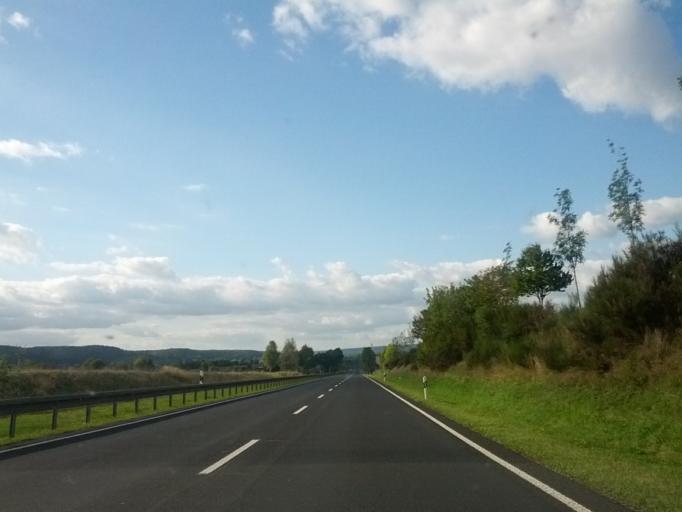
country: DE
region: Thuringia
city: Breitungen
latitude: 50.7641
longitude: 10.3422
